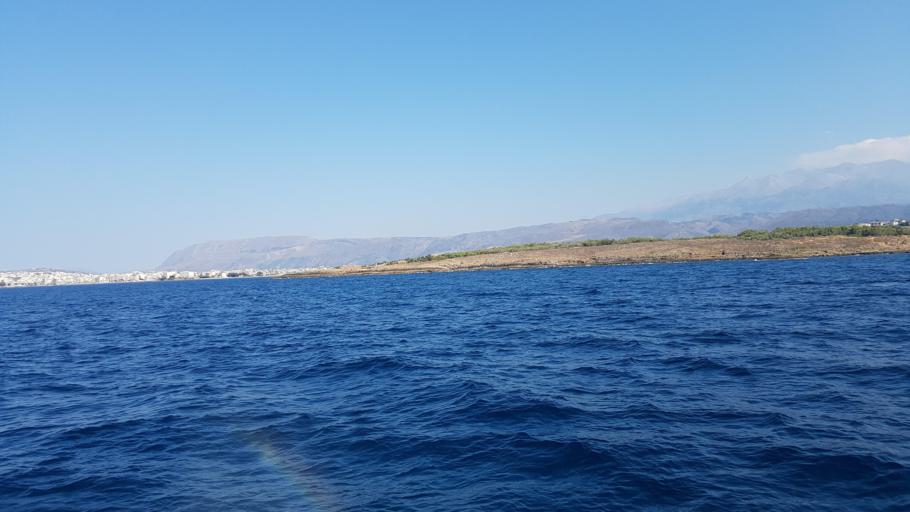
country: GR
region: Crete
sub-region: Nomos Chanias
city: Daratsos
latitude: 35.5215
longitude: 23.9835
